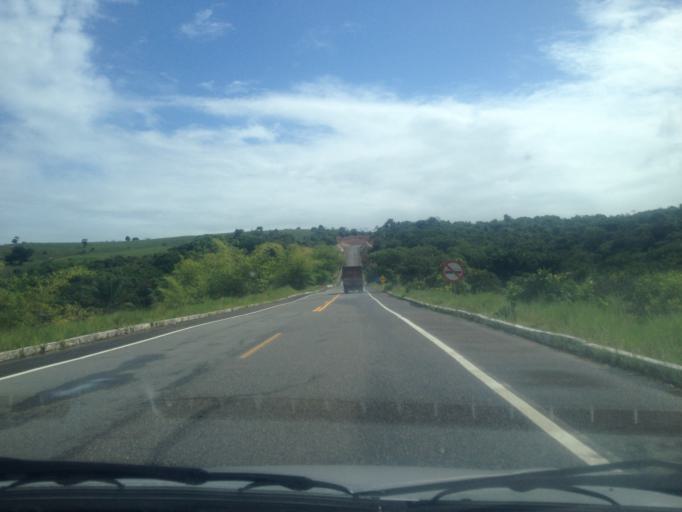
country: BR
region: Sergipe
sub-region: Indiaroba
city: Indiaroba
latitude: -11.5643
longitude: -37.5664
